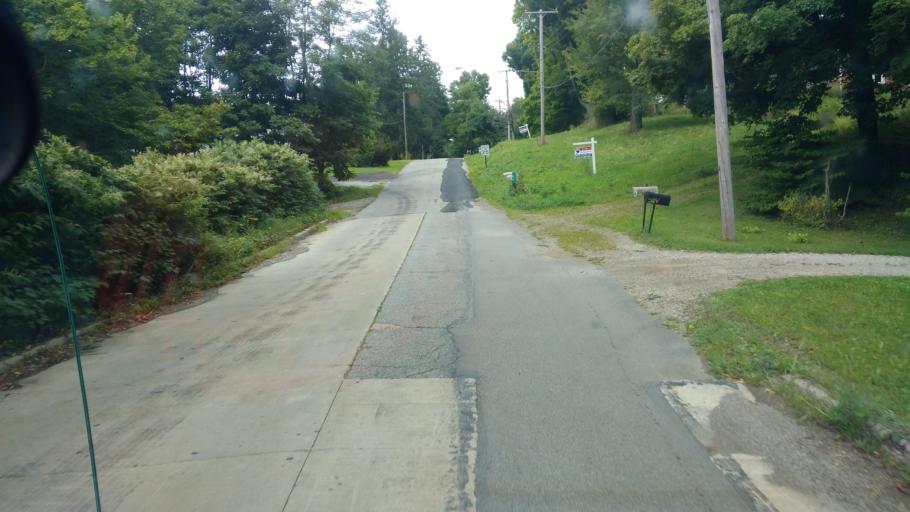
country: US
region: Ohio
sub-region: Ashland County
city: Ashland
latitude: 40.7750
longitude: -82.3639
